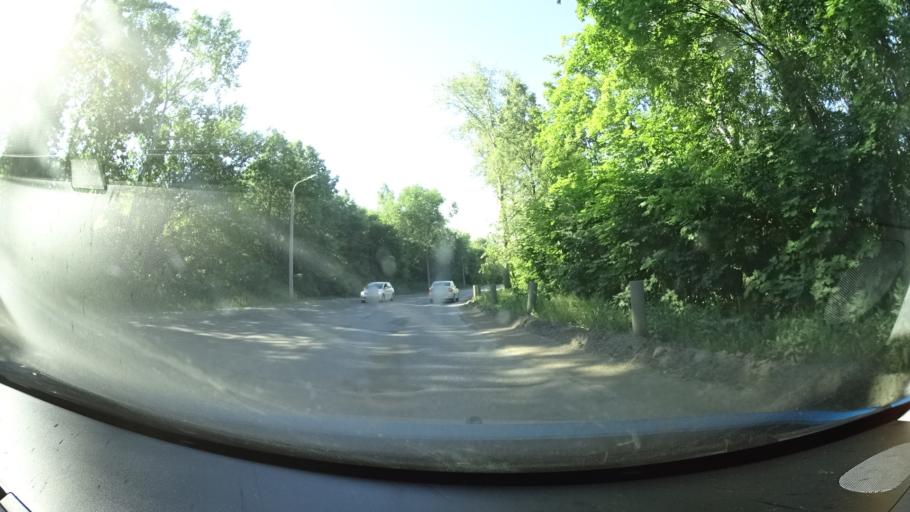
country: RU
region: Bashkortostan
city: Ufa
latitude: 54.8505
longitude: 56.0769
